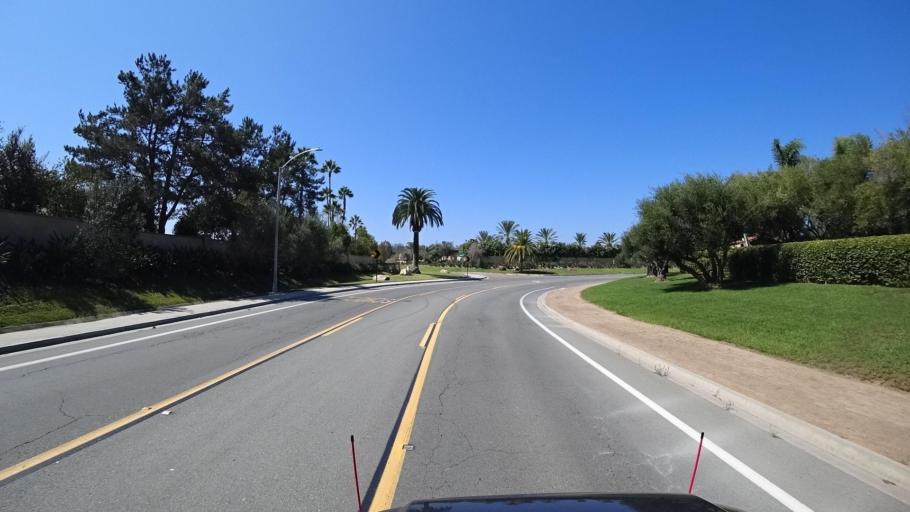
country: US
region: California
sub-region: San Diego County
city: Fairbanks Ranch
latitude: 32.9992
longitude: -117.2001
